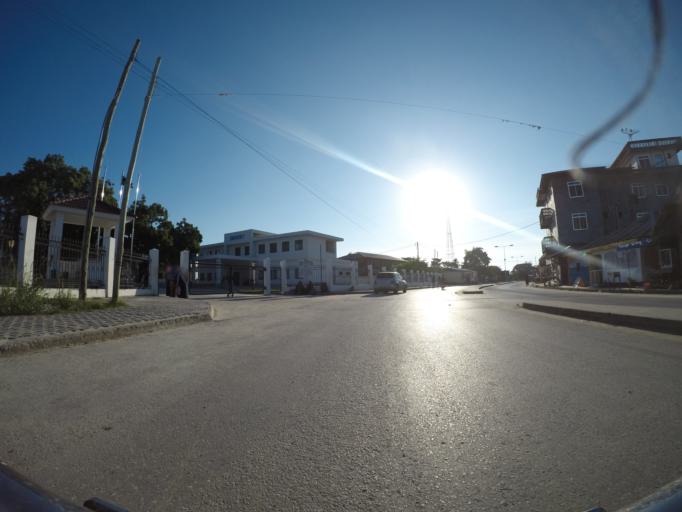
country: TZ
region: Pemba South
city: Uwelini
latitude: -5.3624
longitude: 39.6534
